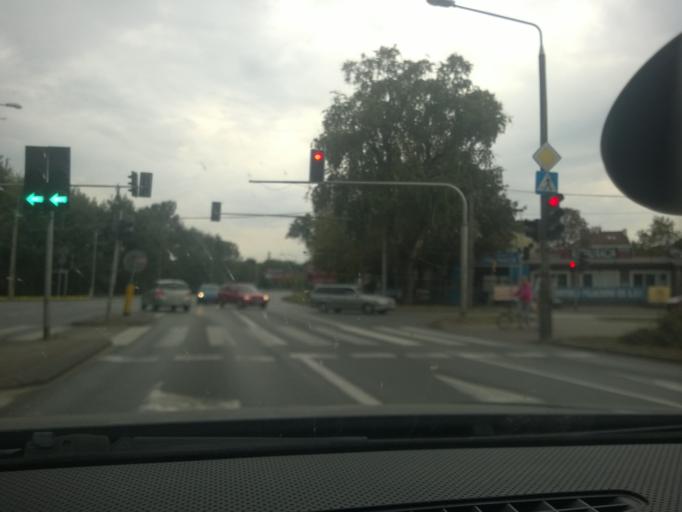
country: PL
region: Masovian Voivodeship
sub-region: Powiat pruszkowski
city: Pruszkow
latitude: 52.1705
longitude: 20.8122
